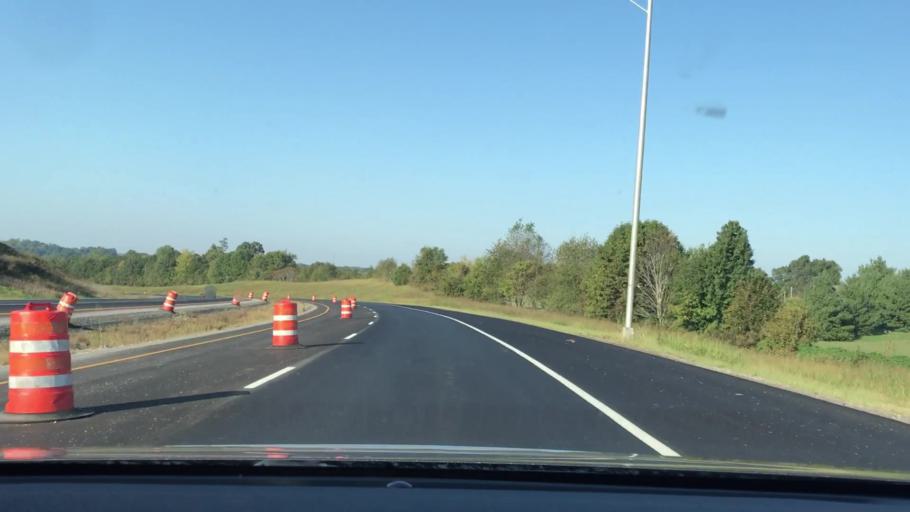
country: US
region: Kentucky
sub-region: Trigg County
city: Cadiz
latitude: 36.8589
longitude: -87.8083
